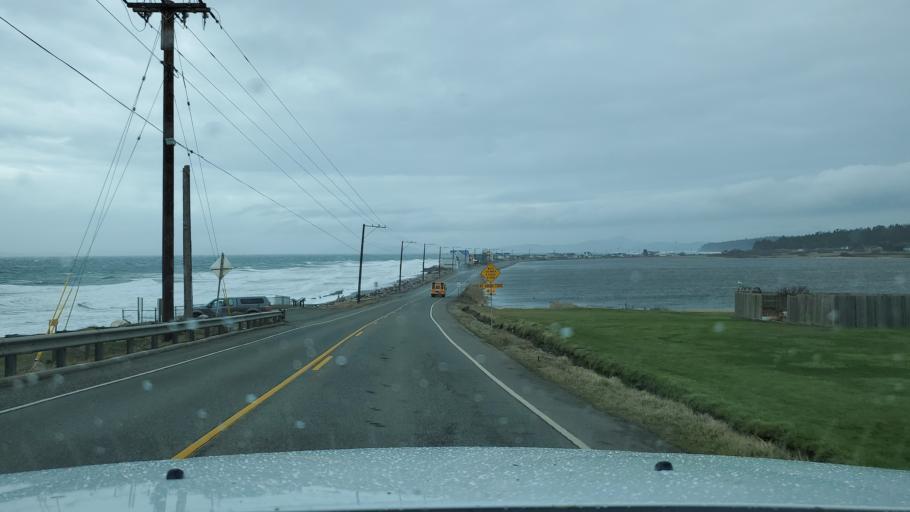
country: US
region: Washington
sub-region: Island County
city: Ault Field
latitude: 48.2972
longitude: -122.7249
